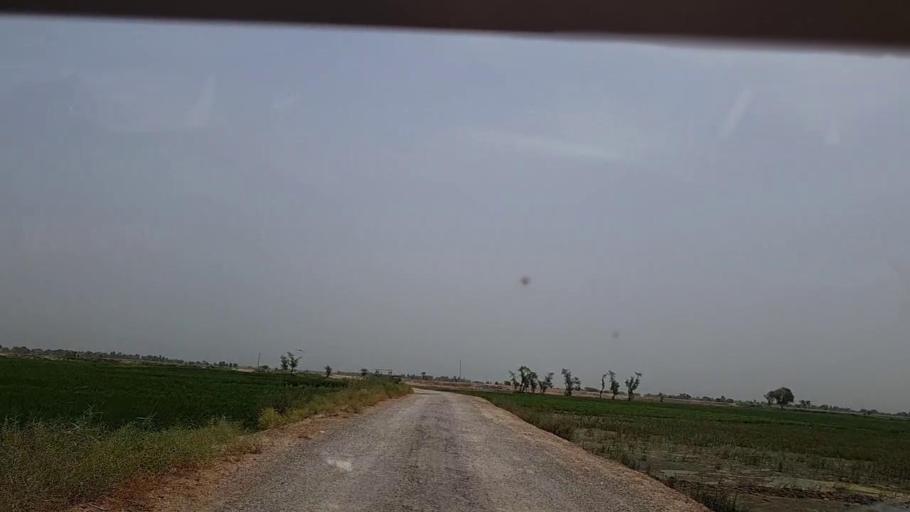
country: PK
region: Sindh
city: Khairpur Nathan Shah
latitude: 27.0158
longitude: 67.6548
